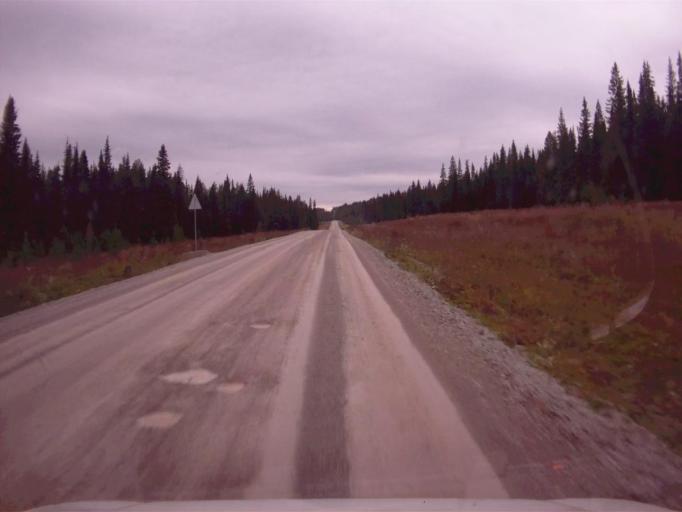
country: RU
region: Chelyabinsk
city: Nyazepetrovsk
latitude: 56.0558
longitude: 59.5507
